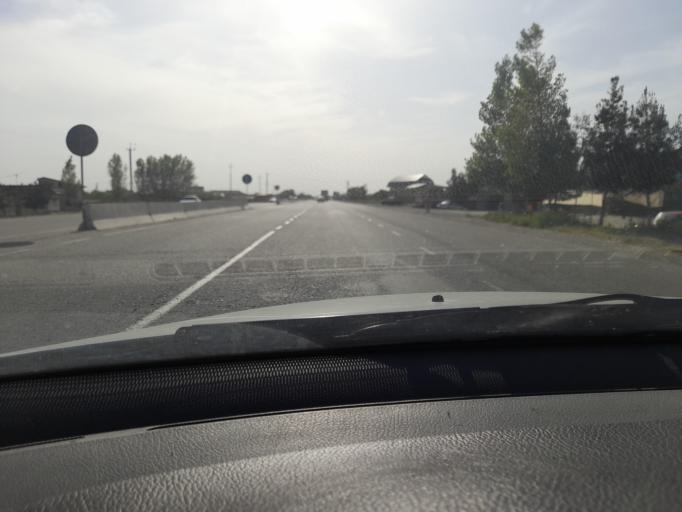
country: UZ
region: Samarqand
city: Kattaqo'rg'on
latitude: 39.9290
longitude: 66.2647
